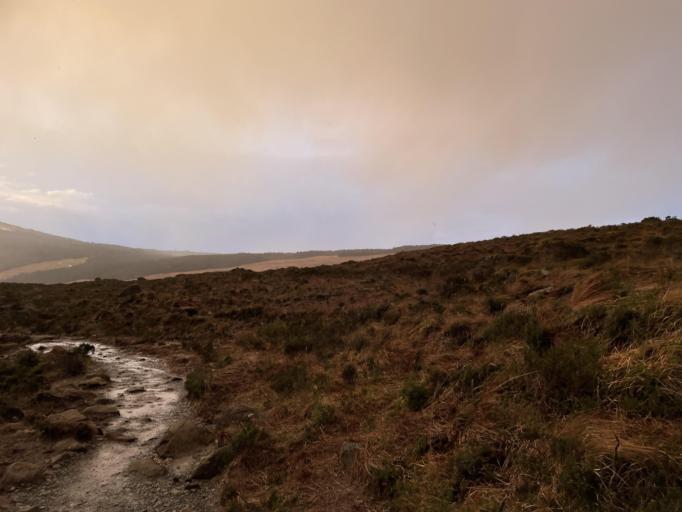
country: GB
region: Scotland
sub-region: Highland
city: Isle of Skye
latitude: 57.2490
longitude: -6.2451
